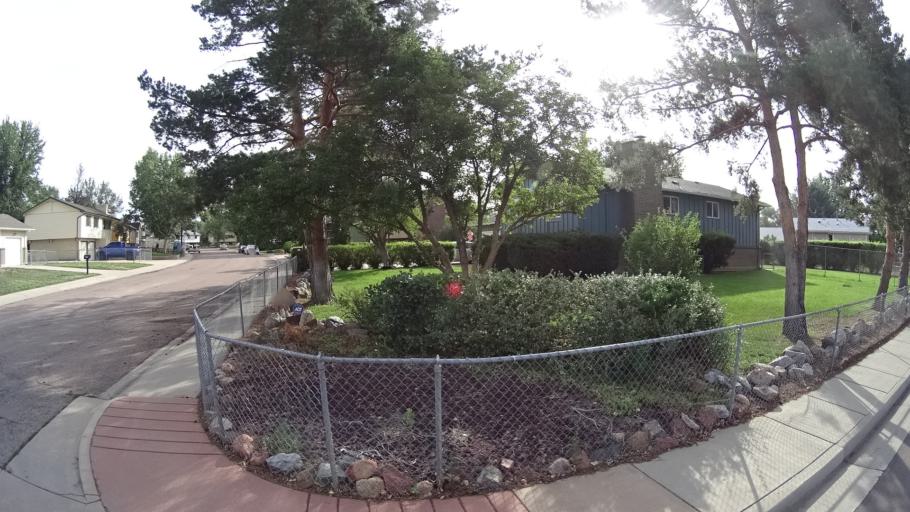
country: US
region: Colorado
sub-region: El Paso County
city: Security-Widefield
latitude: 38.7240
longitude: -104.7011
